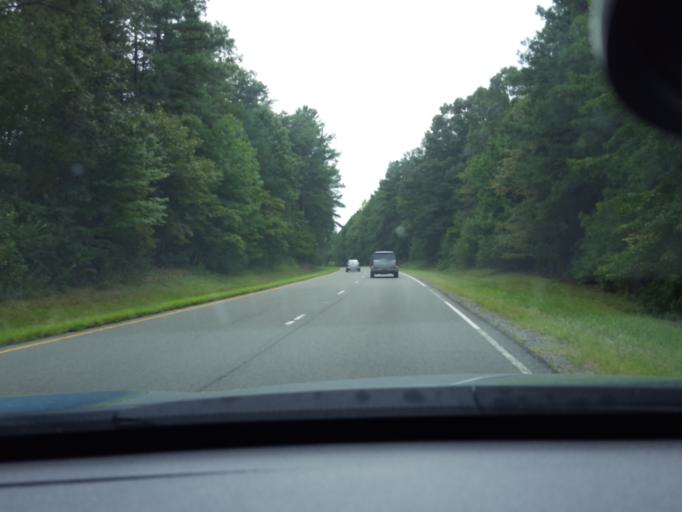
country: US
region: Virginia
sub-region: Caroline County
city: Bowling Green
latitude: 38.0918
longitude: -77.2972
